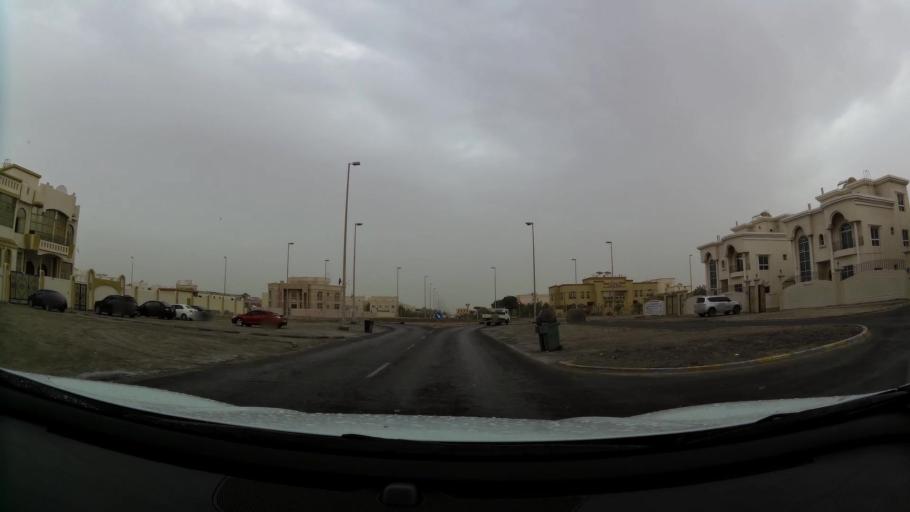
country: AE
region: Abu Dhabi
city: Abu Dhabi
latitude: 24.4125
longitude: 54.5863
